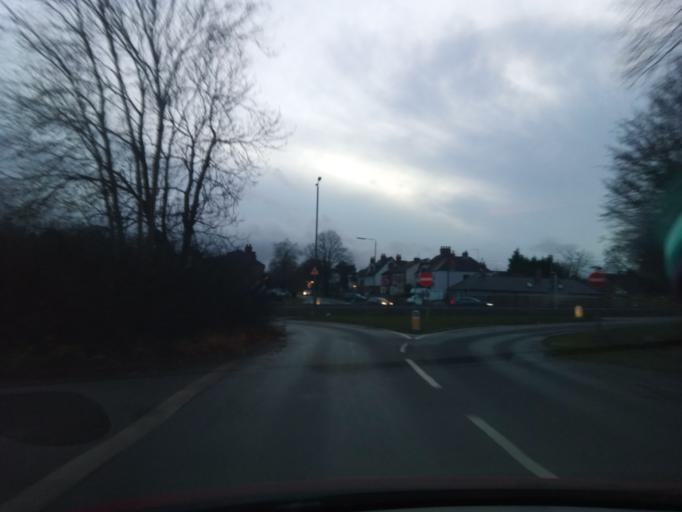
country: GB
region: England
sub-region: Derbyshire
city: Borrowash
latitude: 52.9140
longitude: -1.3766
